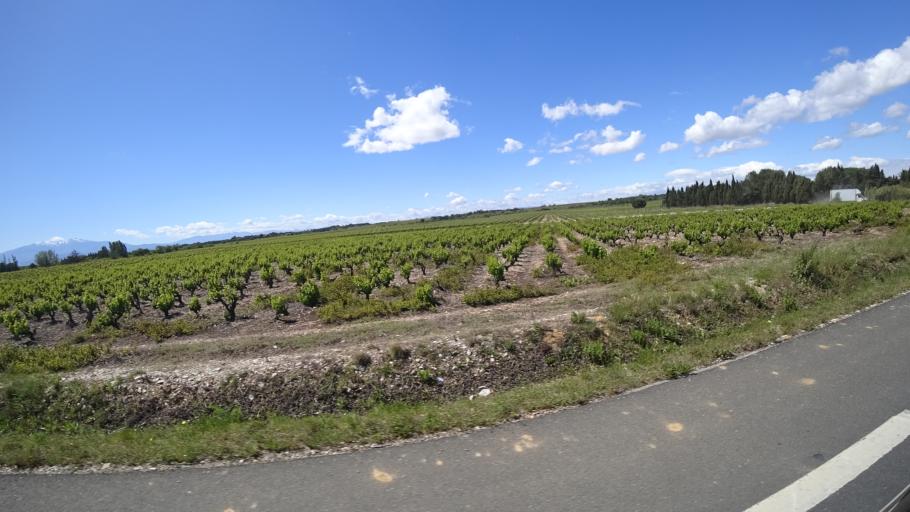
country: FR
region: Languedoc-Roussillon
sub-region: Departement des Pyrenees-Orientales
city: Saint-Nazaire
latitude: 42.6844
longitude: 2.9959
